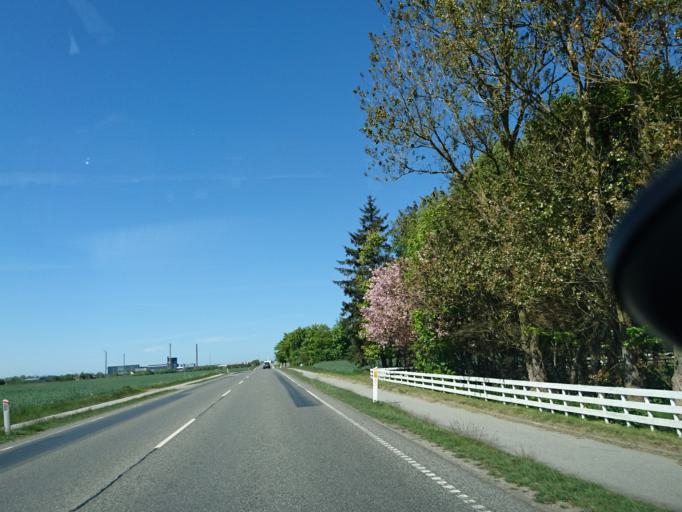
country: DK
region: North Denmark
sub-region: Hjorring Kommune
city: Hjorring
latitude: 57.4563
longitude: 10.0599
